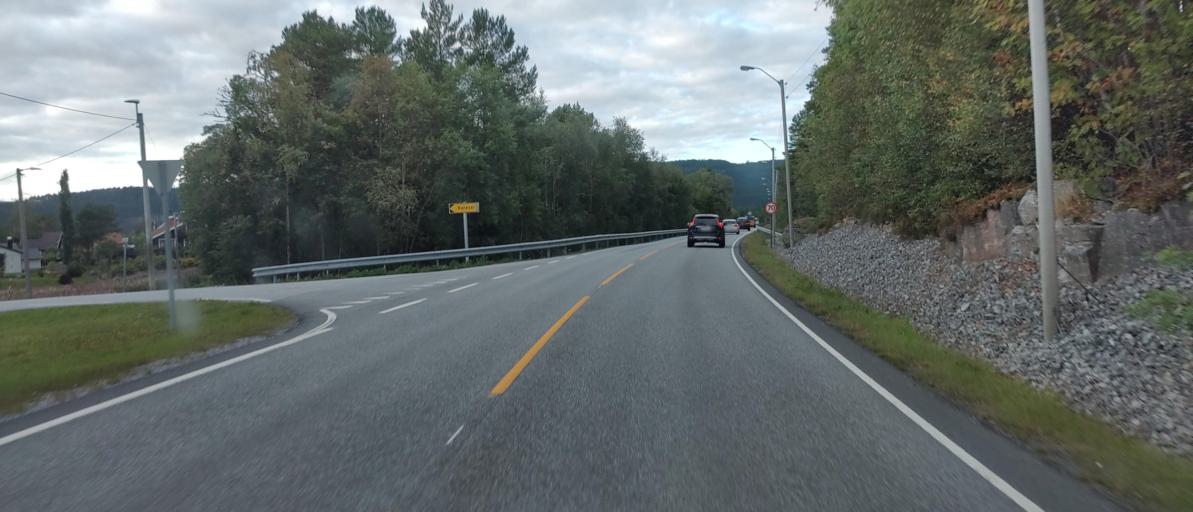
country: NO
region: More og Romsdal
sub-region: Molde
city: Hjelset
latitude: 62.7185
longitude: 7.4280
